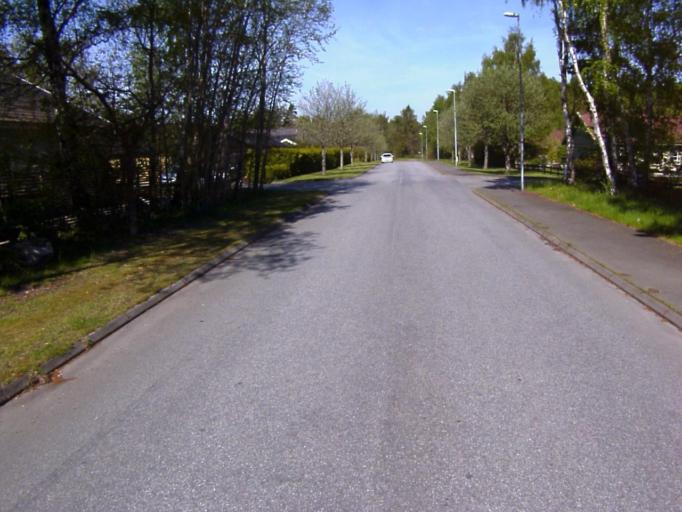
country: SE
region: Skane
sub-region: Kristianstads Kommun
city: Onnestad
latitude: 55.9416
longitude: 13.9864
